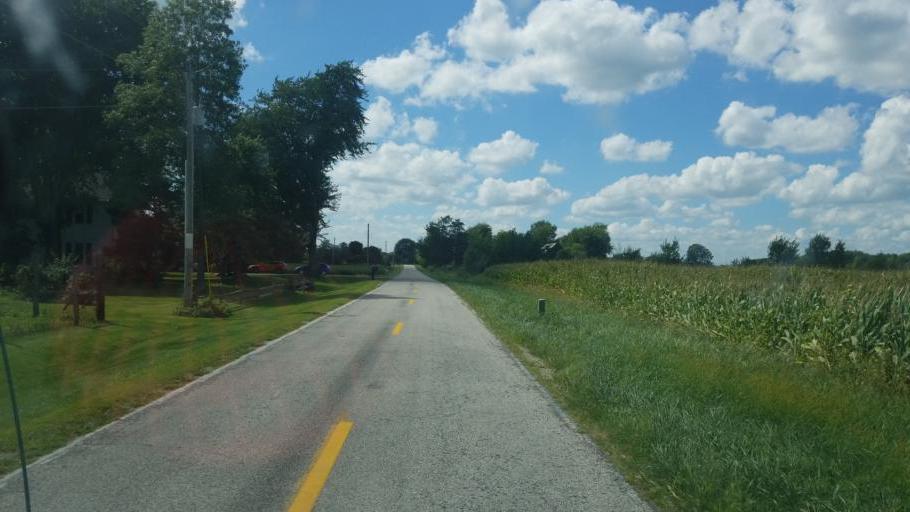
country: US
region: Ohio
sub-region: Union County
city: Richwood
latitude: 40.3501
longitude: -83.2262
